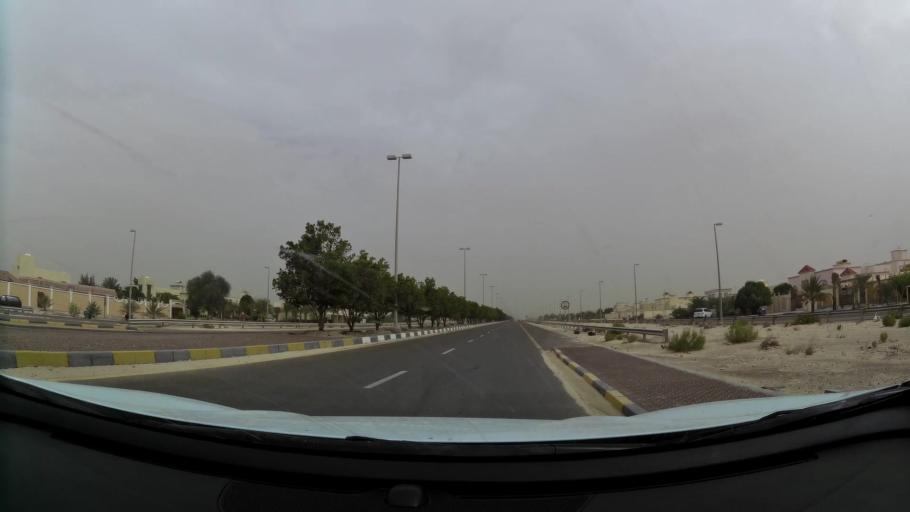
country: AE
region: Abu Dhabi
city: Abu Dhabi
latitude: 24.3765
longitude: 54.7173
